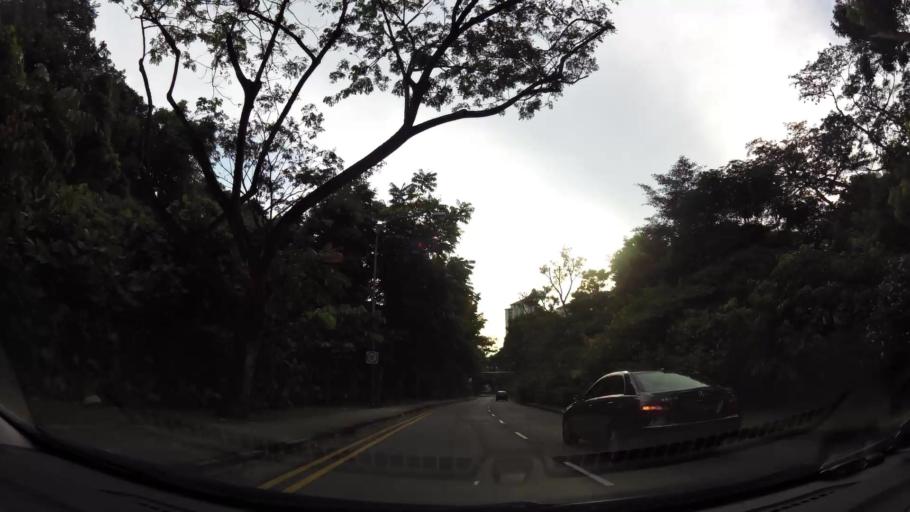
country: SG
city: Singapore
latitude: 1.2740
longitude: 103.8140
